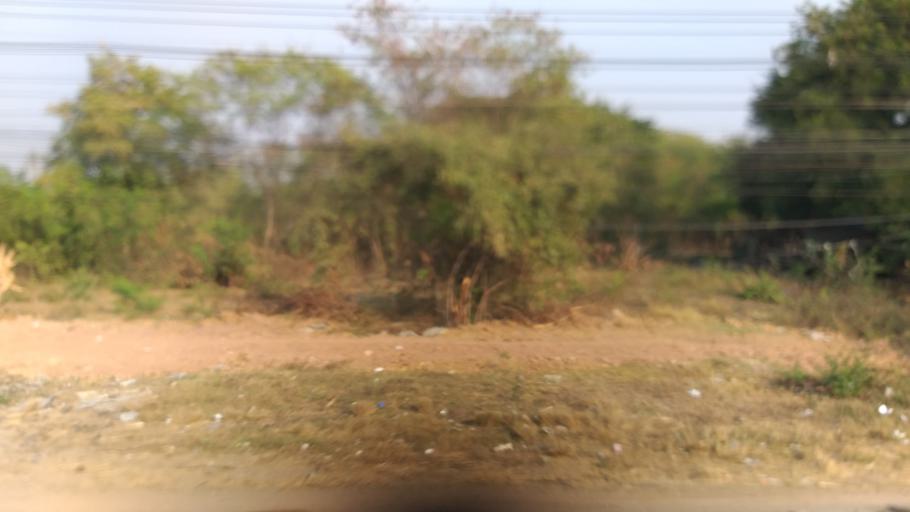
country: TH
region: Khon Kaen
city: Nam Phong
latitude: 16.7080
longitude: 102.8053
